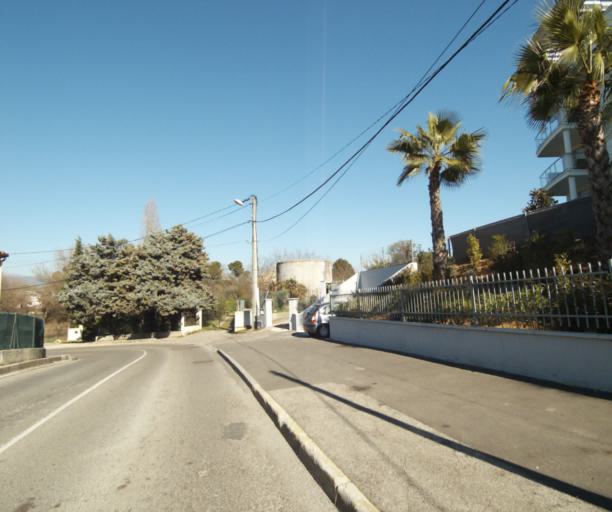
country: FR
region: Provence-Alpes-Cote d'Azur
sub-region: Departement des Alpes-Maritimes
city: Biot
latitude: 43.5978
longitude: 7.0944
